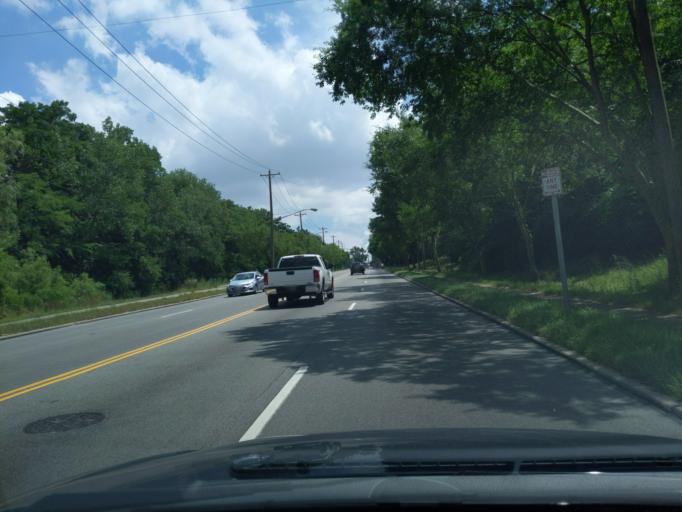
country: US
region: Ohio
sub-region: Hamilton County
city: Saint Bernard
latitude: 39.1377
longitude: -84.5229
